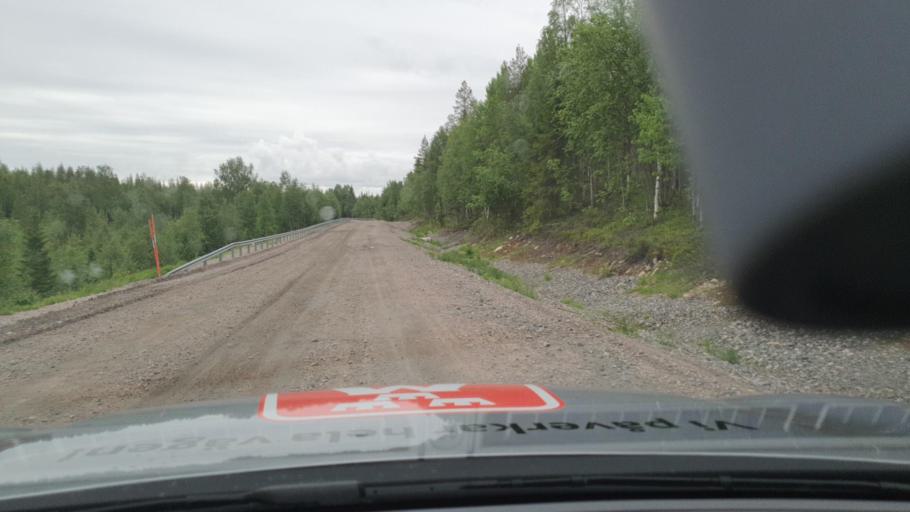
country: SE
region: Norrbotten
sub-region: Overtornea Kommun
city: OEvertornea
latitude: 66.5108
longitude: 23.4037
